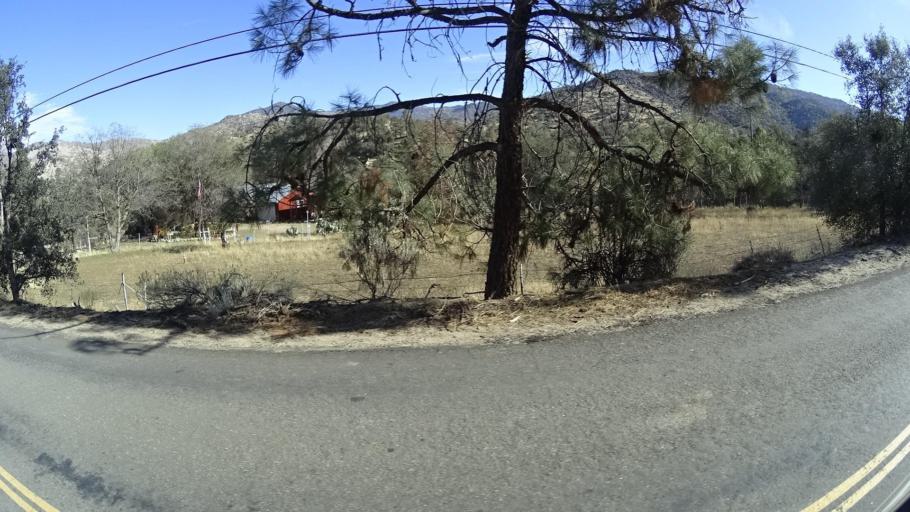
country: US
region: California
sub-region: Kern County
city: Bodfish
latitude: 35.5017
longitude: -118.5222
